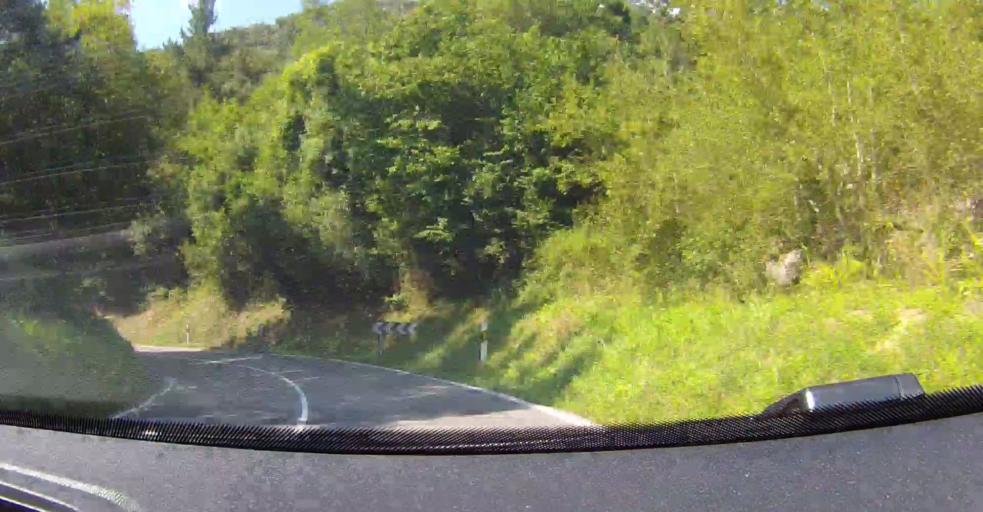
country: ES
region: Basque Country
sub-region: Bizkaia
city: Kortezubi
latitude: 43.3605
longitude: -2.6481
